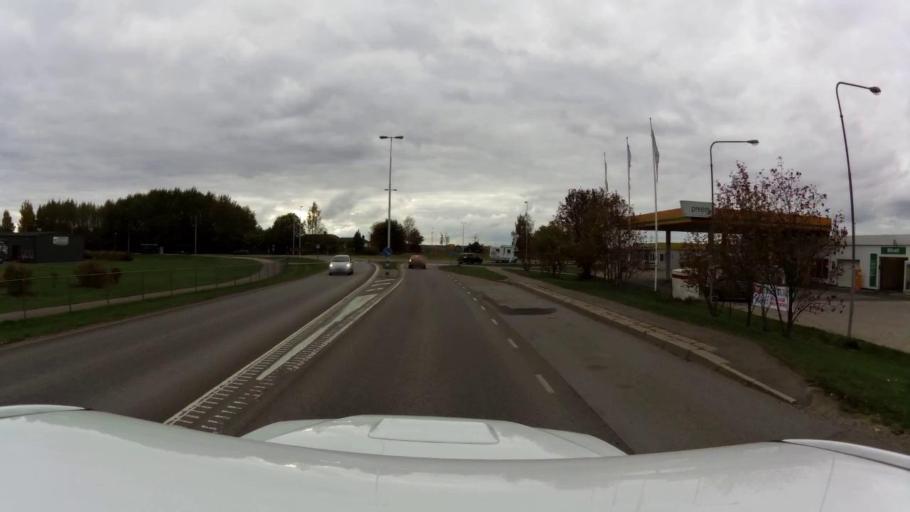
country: SE
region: OEstergoetland
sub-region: Linkopings Kommun
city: Ljungsbro
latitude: 58.4909
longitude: 15.4993
